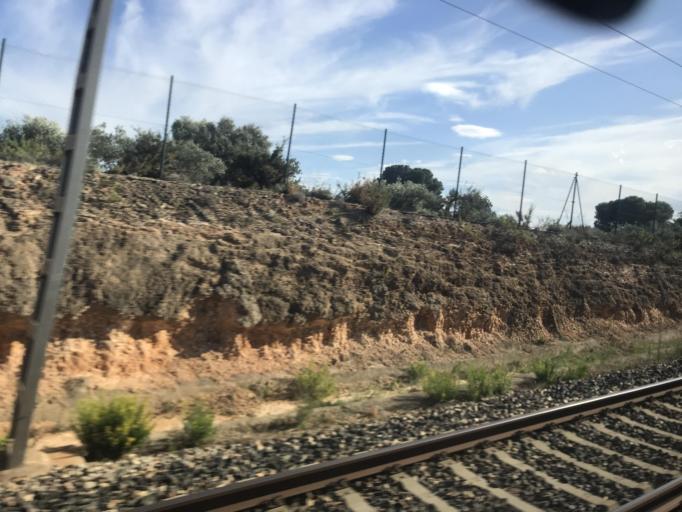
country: ES
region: Catalonia
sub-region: Provincia de Tarragona
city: l'Ametlla de Mar
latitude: 40.8640
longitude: 0.7755
